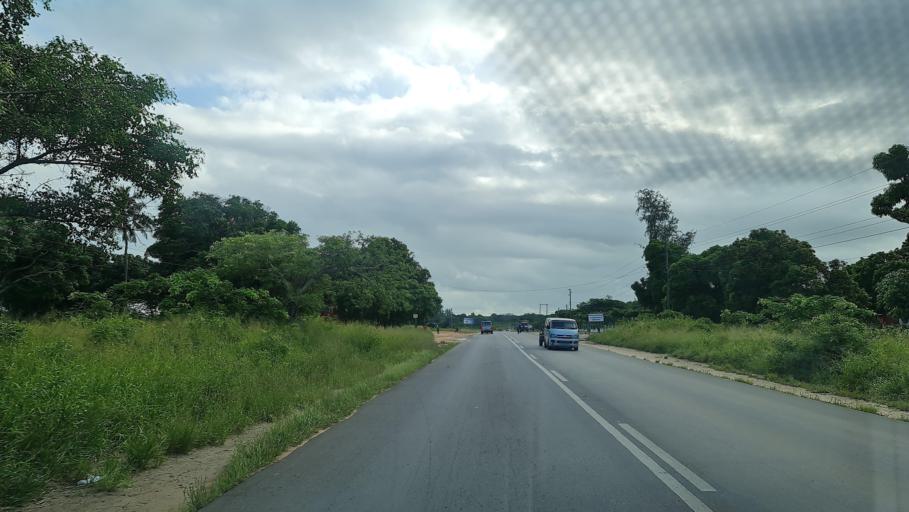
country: MZ
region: Maputo
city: Manhica
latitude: -25.4131
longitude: 32.7406
